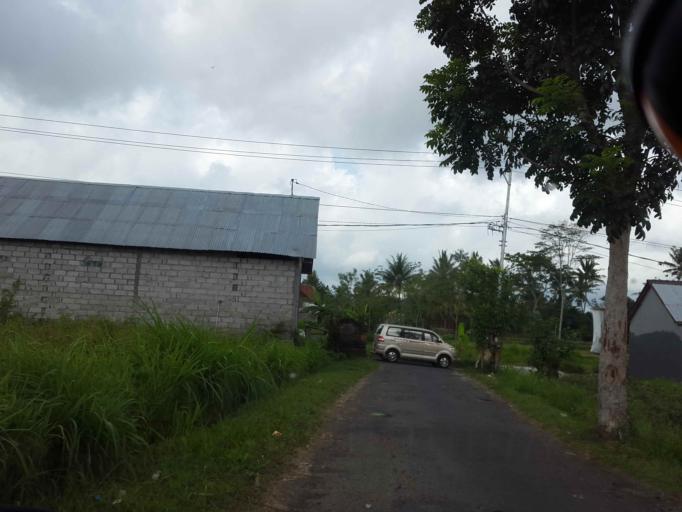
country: ID
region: Bali
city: Banjar Kelodan
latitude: -8.4929
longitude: 115.3683
